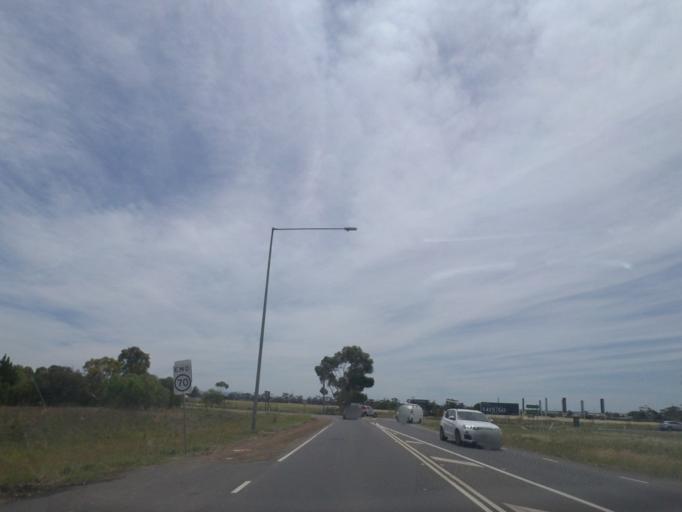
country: AU
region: Victoria
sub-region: Melton
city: Rockbank
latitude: -37.7416
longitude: 144.7010
